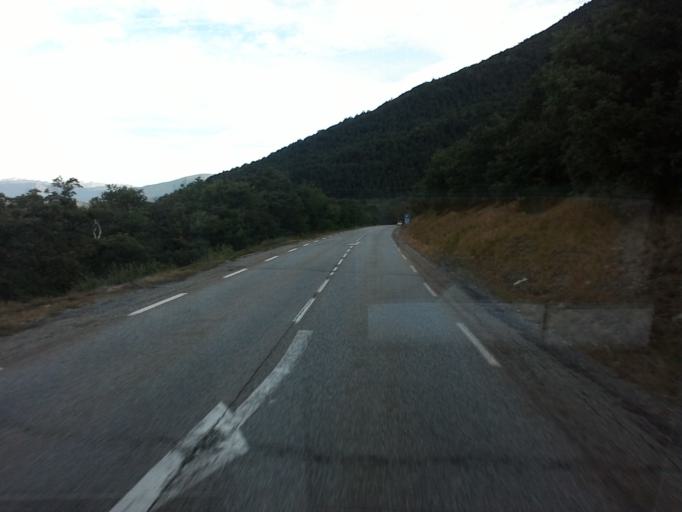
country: FR
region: Rhone-Alpes
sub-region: Departement de l'Isere
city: La Mure
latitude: 44.8334
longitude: 5.8889
